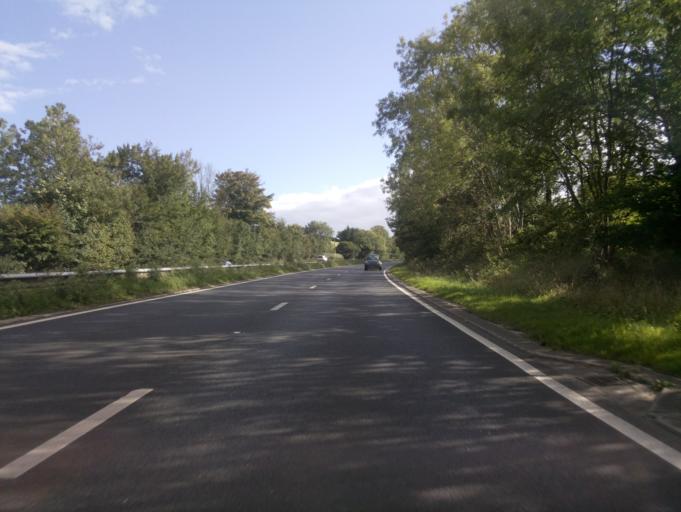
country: GB
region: England
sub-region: Devon
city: Buckfastleigh
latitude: 50.4532
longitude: -3.7907
